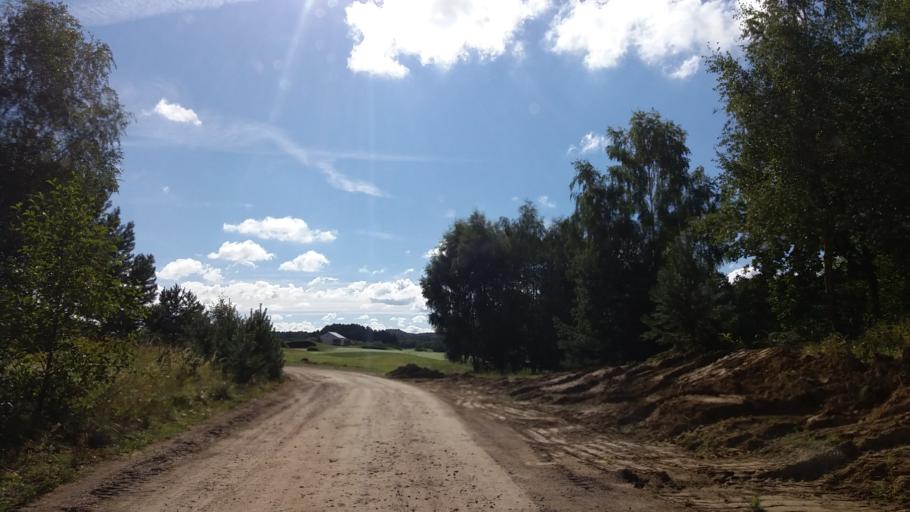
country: PL
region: West Pomeranian Voivodeship
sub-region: Powiat choszczenski
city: Krzecin
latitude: 53.1346
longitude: 15.4847
